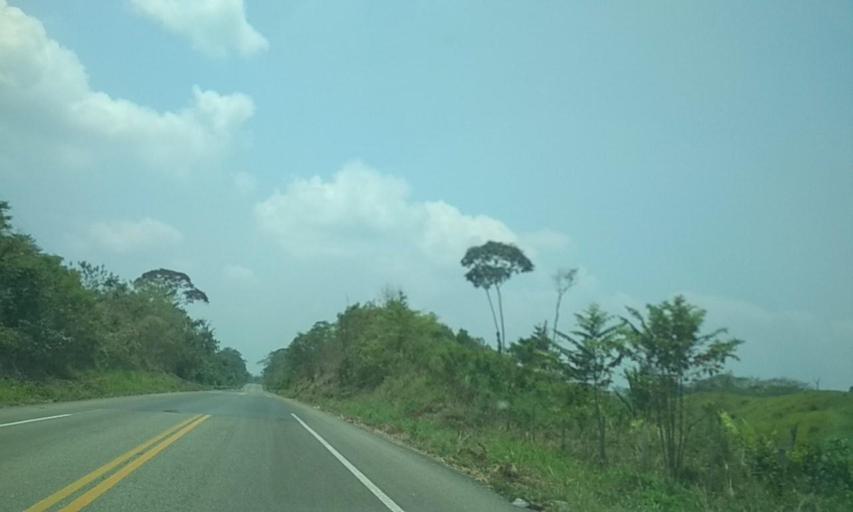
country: MX
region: Tabasco
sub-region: Huimanguillo
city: Francisco Rueda
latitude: 17.6783
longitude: -93.8824
